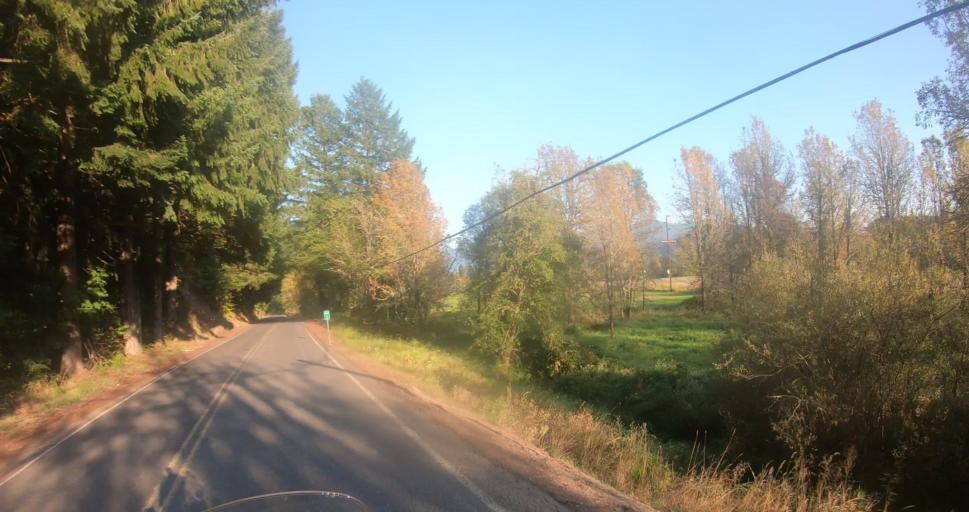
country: US
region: Washington
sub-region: Lewis County
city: Morton
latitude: 46.5359
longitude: -121.9499
